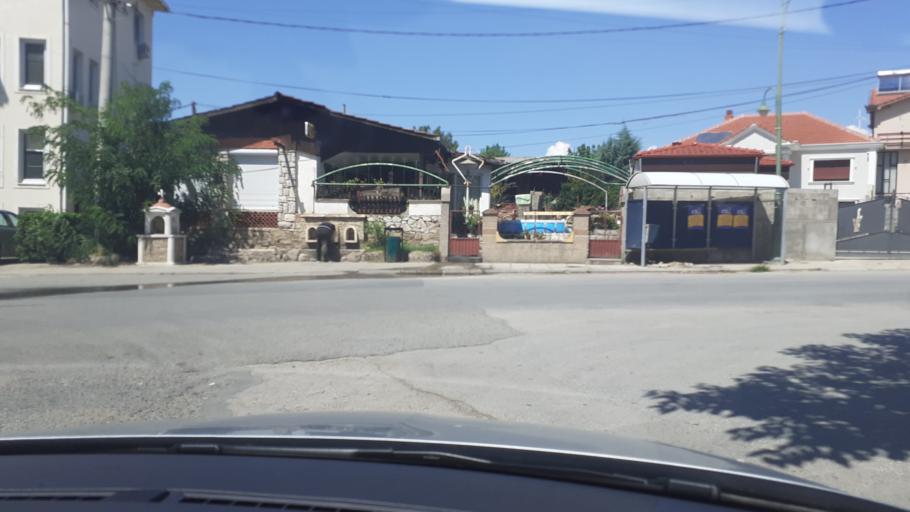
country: MK
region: Bogdanci
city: Bogdanci
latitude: 41.1994
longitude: 22.5716
